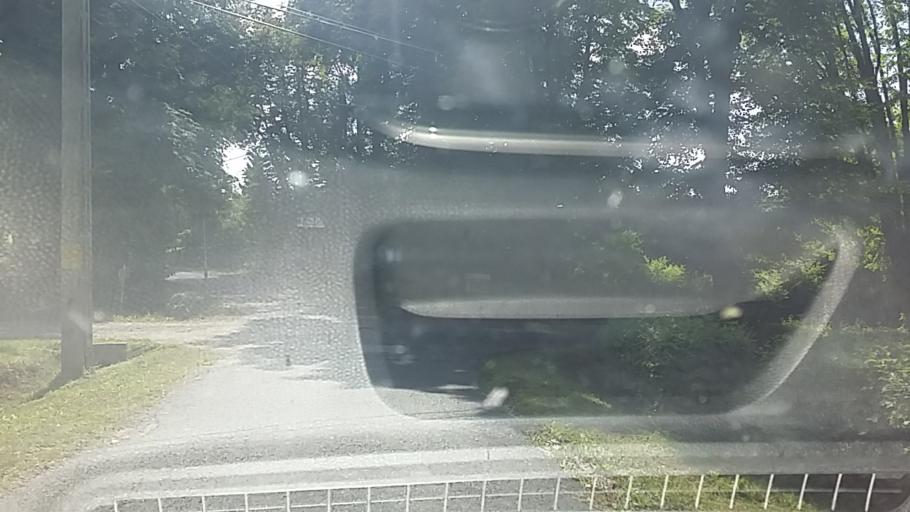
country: HU
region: Zala
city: Becsehely
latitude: 46.5192
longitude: 16.7334
